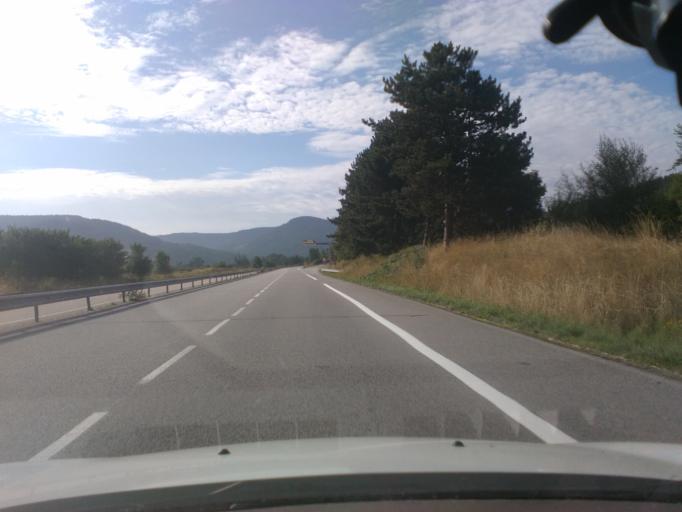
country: FR
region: Lorraine
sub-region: Departement des Vosges
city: Saint-Etienne-les-Remiremont
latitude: 48.0057
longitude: 6.6141
